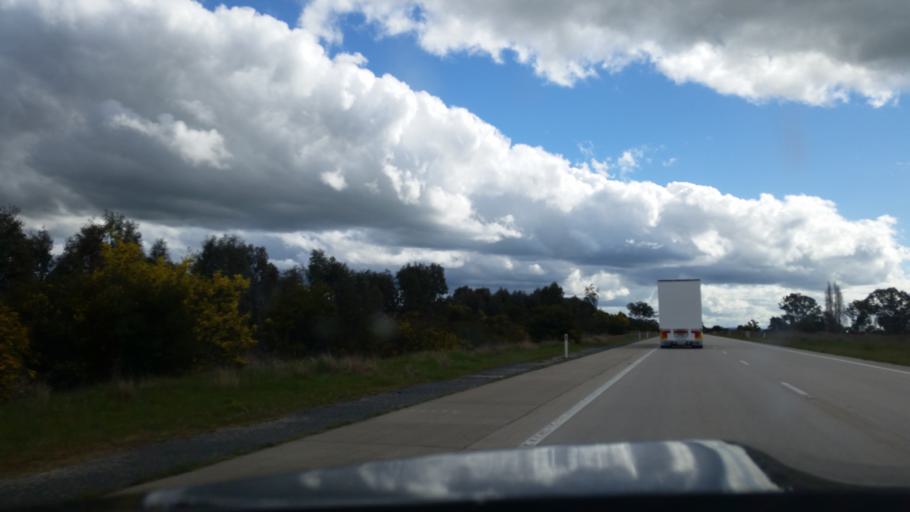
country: AU
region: New South Wales
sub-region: Greater Hume Shire
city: Jindera
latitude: -35.9252
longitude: 147.0250
